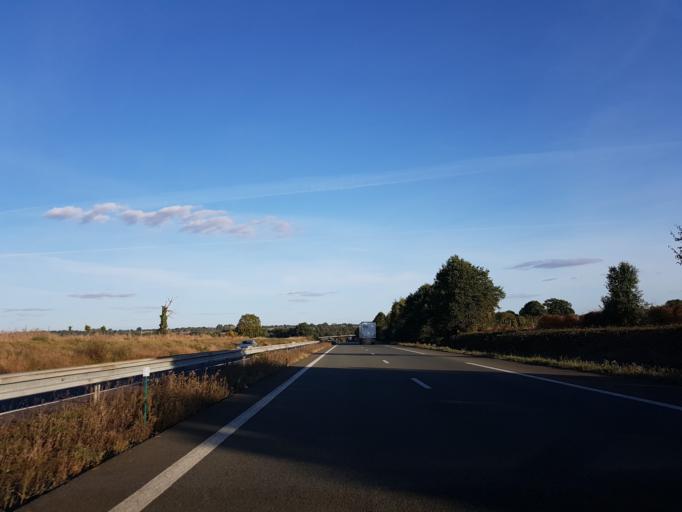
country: FR
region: Pays de la Loire
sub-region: Departement de la Mayenne
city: Argentre
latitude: 48.0799
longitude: -0.6570
